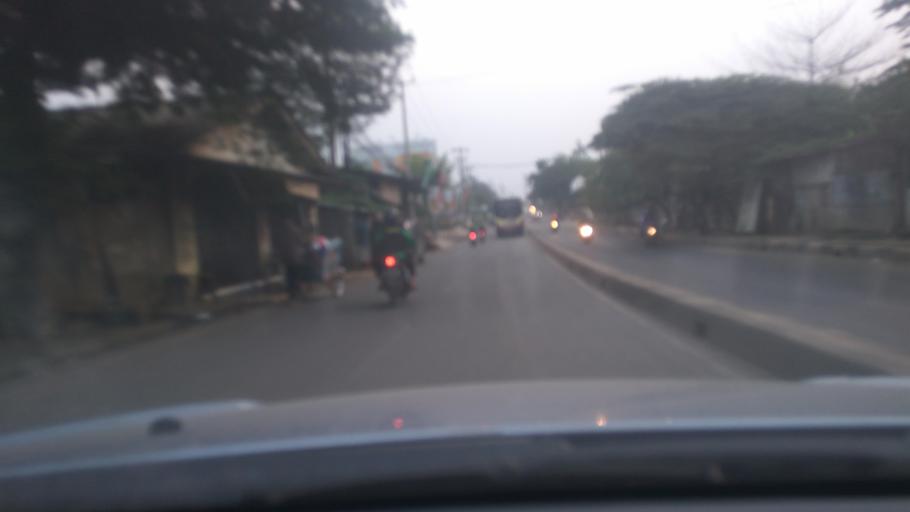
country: ID
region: West Java
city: Pamulang
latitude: -6.3532
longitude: 106.7496
